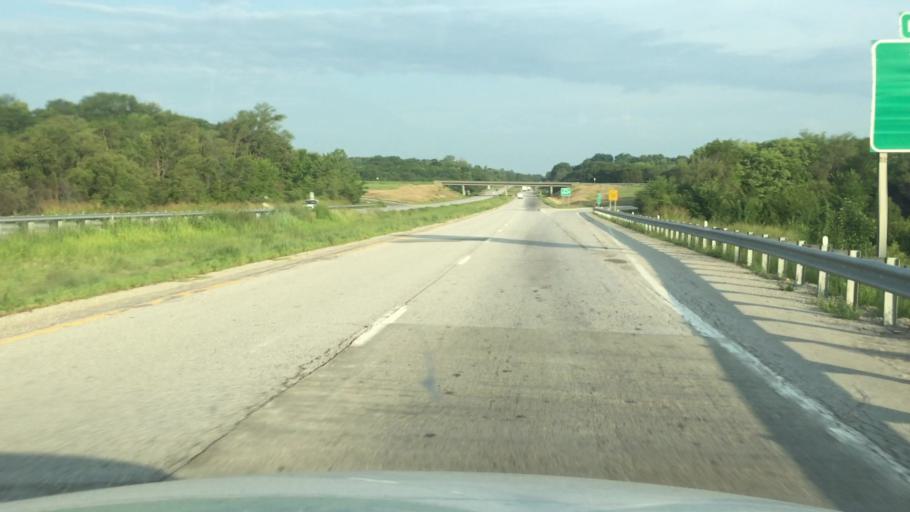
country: US
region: Missouri
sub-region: Buchanan County
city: Saint Joseph
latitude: 39.7154
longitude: -94.8152
